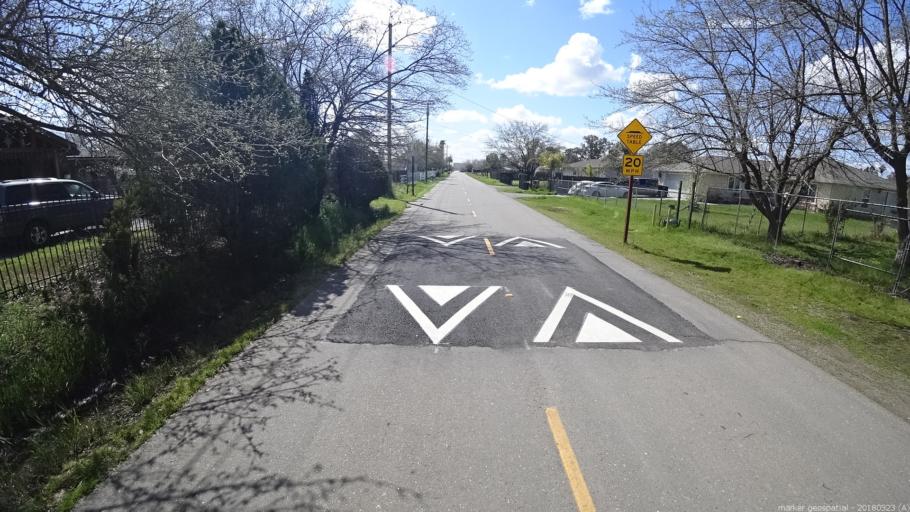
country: US
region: California
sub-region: Sacramento County
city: Rio Linda
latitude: 38.6779
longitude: -121.4152
